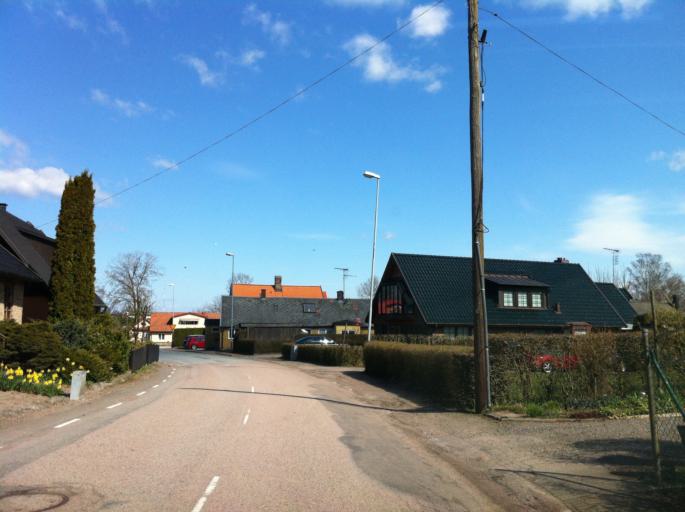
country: SE
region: Skane
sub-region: Helsingborg
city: Glumslov
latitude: 55.9188
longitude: 12.8678
